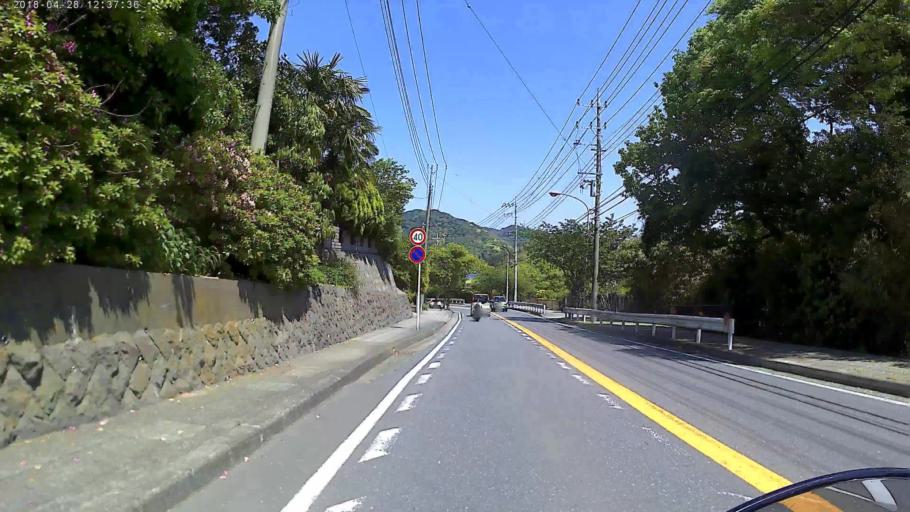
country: JP
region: Kanagawa
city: Hayama
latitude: 35.2656
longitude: 139.6009
